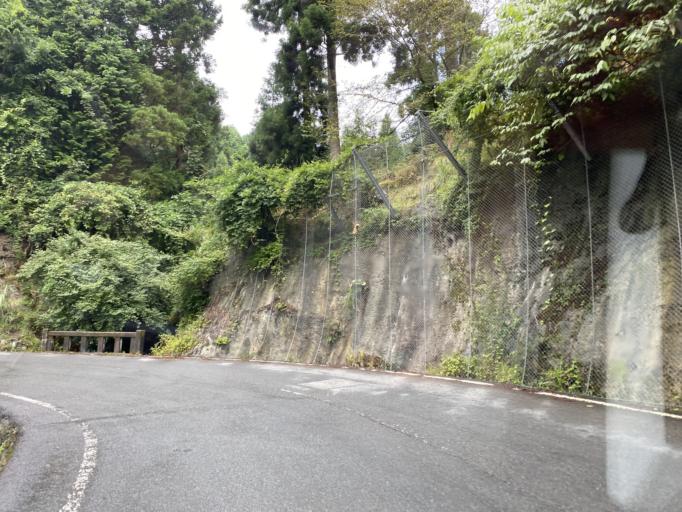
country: JP
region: Kyoto
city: Fukuchiyama
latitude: 35.3036
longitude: 134.9415
